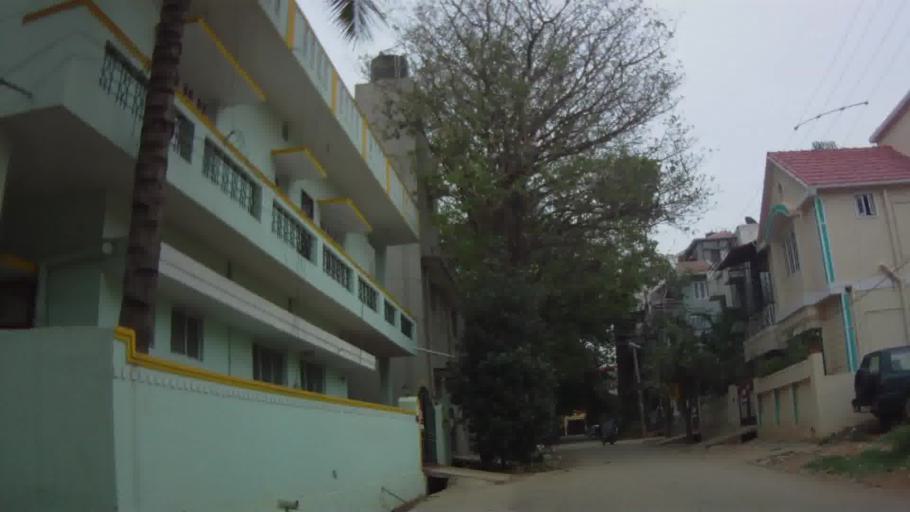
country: IN
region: Karnataka
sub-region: Bangalore Urban
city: Bangalore
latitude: 12.9616
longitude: 77.7113
